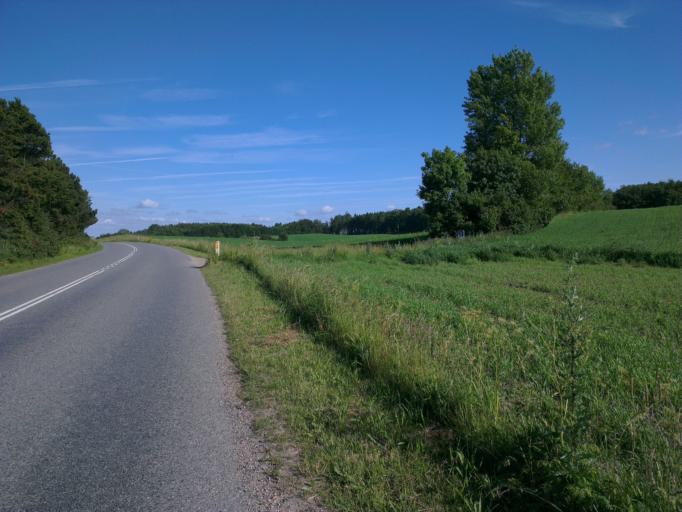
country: DK
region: Capital Region
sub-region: Frederikssund Kommune
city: Skibby
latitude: 55.7878
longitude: 11.9536
